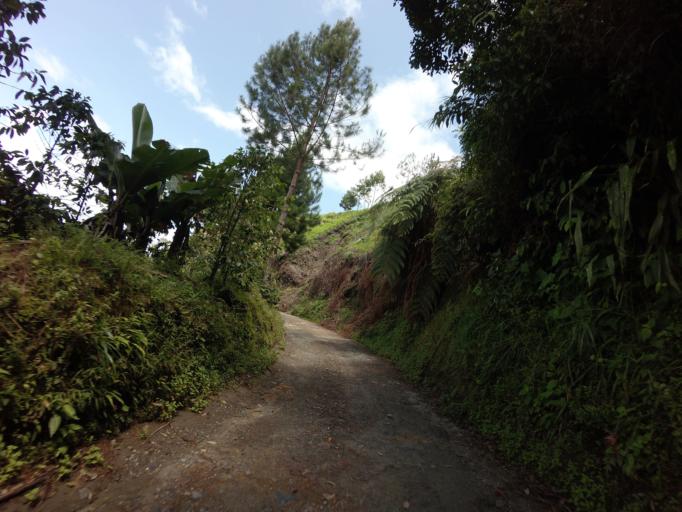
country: CO
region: Caldas
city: Pensilvania
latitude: 5.4643
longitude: -75.1699
